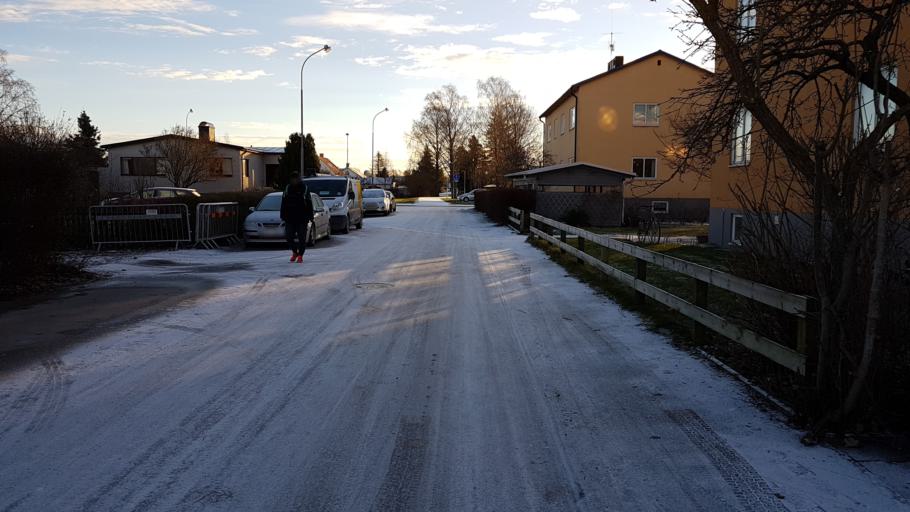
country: SE
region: Gotland
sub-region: Gotland
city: Visby
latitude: 57.6335
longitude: 18.3044
